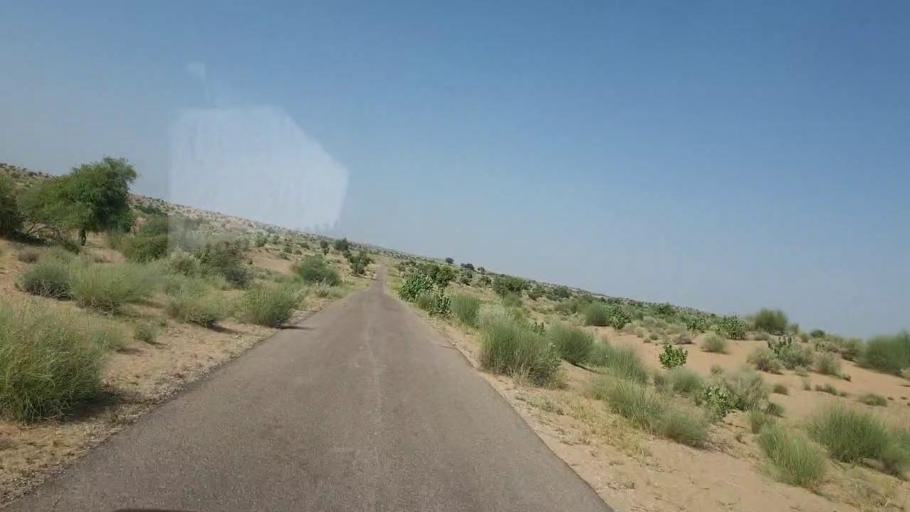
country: PK
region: Sindh
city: Chor
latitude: 25.6283
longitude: 70.3171
